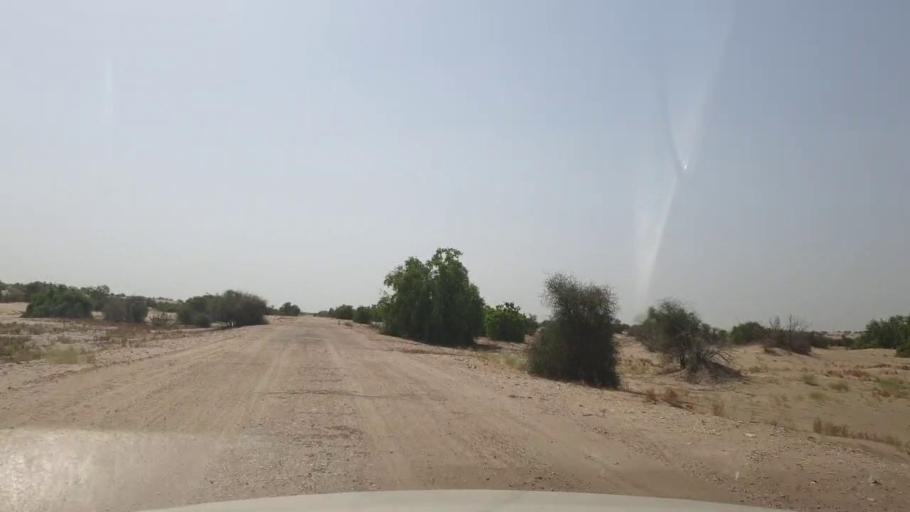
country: PK
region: Sindh
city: Rohri
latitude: 27.4518
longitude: 69.2278
